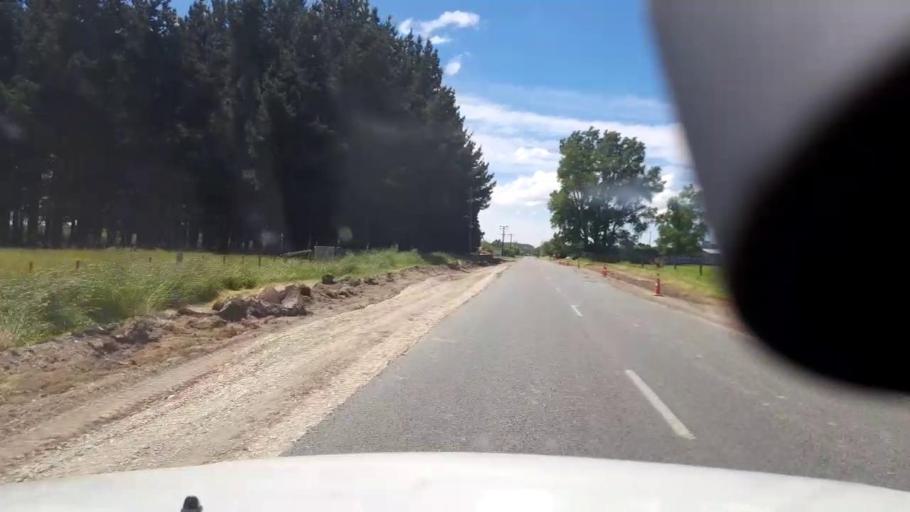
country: NZ
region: Canterbury
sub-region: Timaru District
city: Pleasant Point
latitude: -44.2760
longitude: 171.2513
